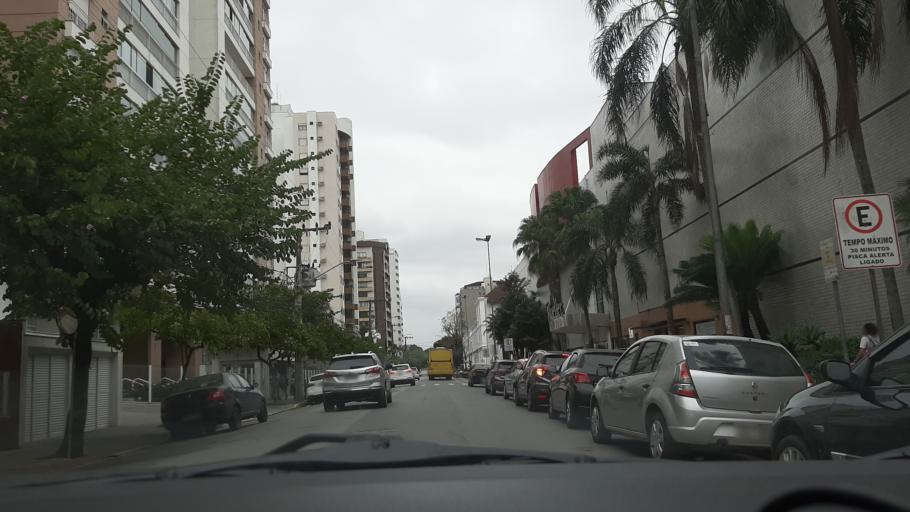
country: BR
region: Santa Catarina
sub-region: Joinville
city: Joinville
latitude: -26.3040
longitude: -48.8484
